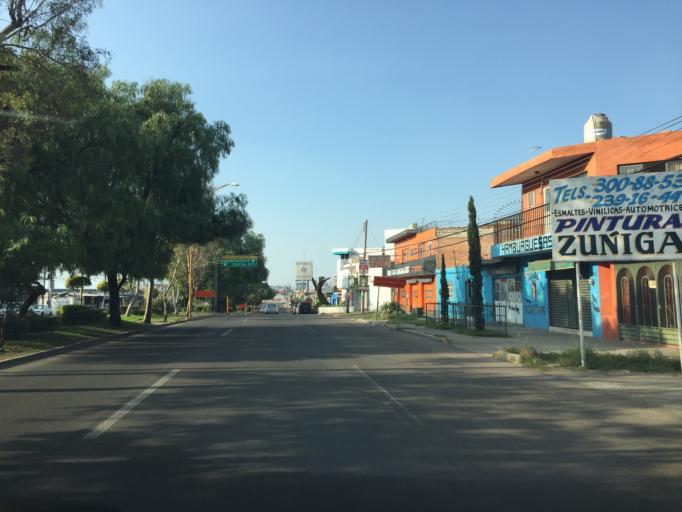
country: MX
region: Aguascalientes
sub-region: Aguascalientes
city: La Loma de los Negritos
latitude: 21.8647
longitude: -102.3175
